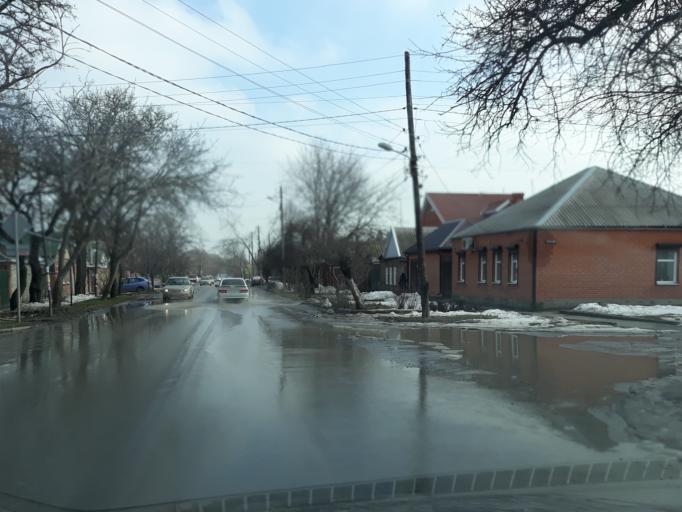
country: RU
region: Rostov
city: Taganrog
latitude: 47.2136
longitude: 38.9048
